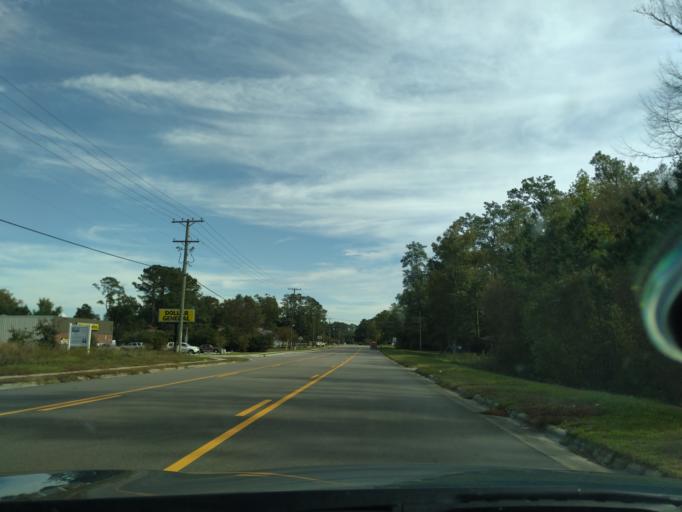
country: US
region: North Carolina
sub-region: Beaufort County
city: River Road
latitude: 35.5060
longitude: -76.9928
